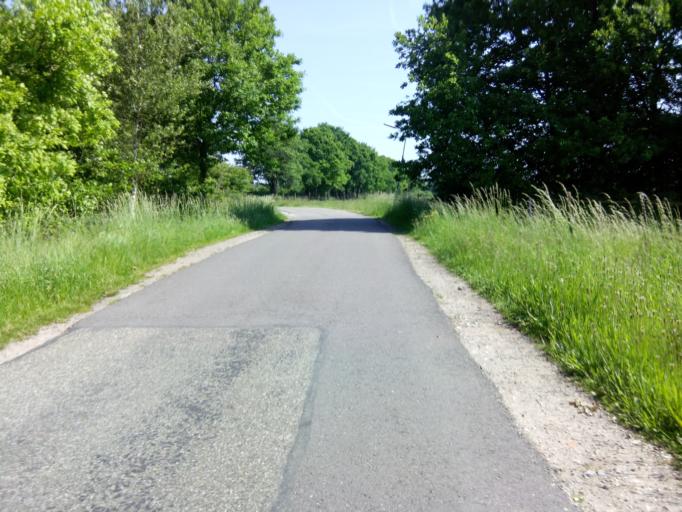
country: NL
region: Utrecht
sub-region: Gemeente Utrechtse Heuvelrug
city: Maarsbergen
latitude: 52.0464
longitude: 5.4156
